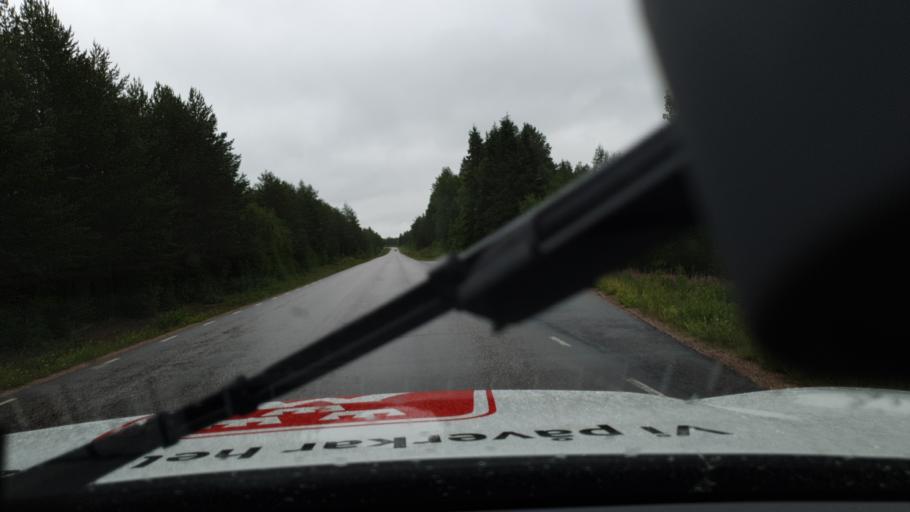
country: SE
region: Norrbotten
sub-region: Overtornea Kommun
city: OEvertornea
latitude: 66.4748
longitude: 23.6812
